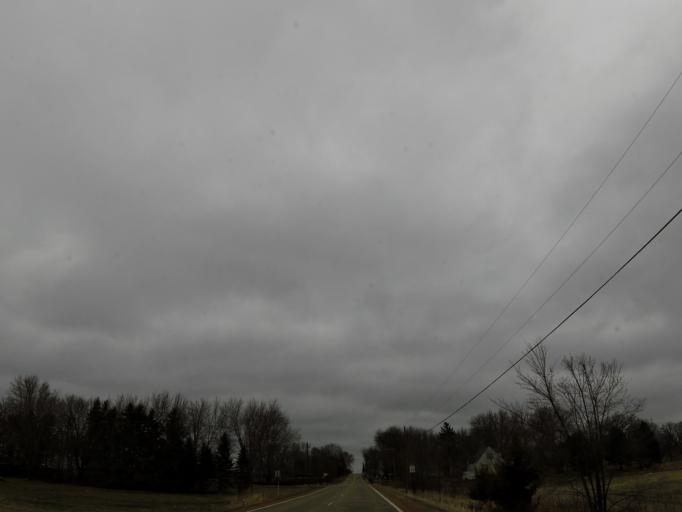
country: US
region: Minnesota
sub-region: Scott County
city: Shakopee
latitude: 44.7252
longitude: -93.5418
